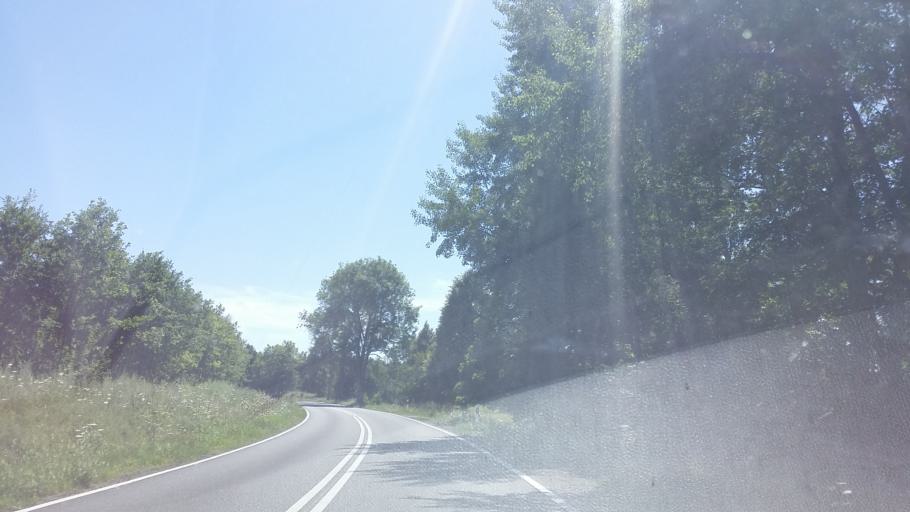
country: PL
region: West Pomeranian Voivodeship
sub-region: Powiat lobeski
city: Wegorzyno
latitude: 53.4977
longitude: 15.5750
